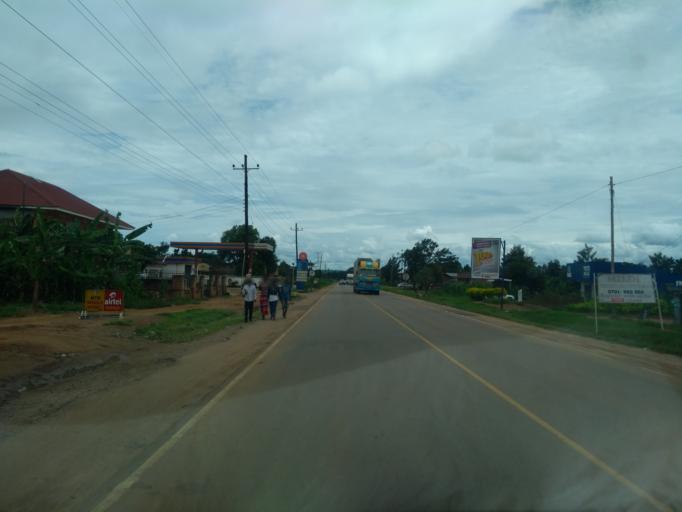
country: UG
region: Central Region
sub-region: Butambala District
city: Gombe
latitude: -0.0161
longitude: 32.0288
